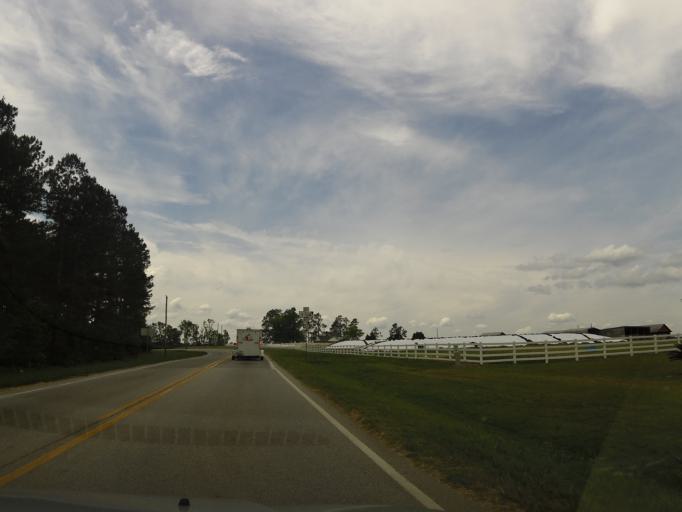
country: US
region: Georgia
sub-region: Emanuel County
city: Swainsboro
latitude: 32.5241
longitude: -82.2975
